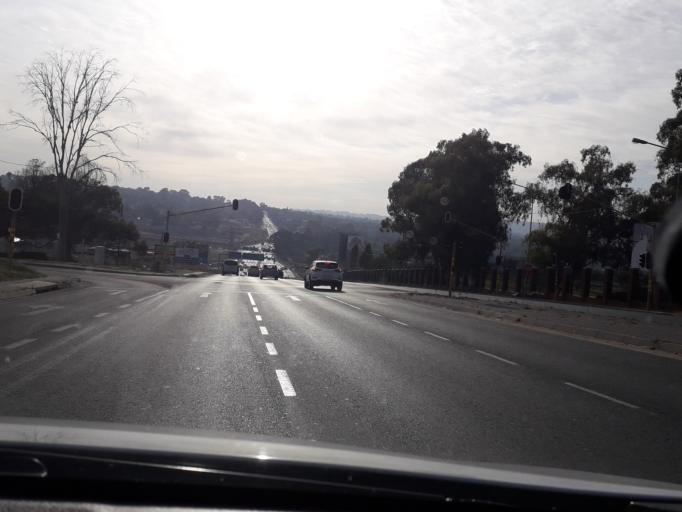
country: ZA
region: Gauteng
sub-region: City of Johannesburg Metropolitan Municipality
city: Modderfontein
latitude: -26.1489
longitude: 28.1258
